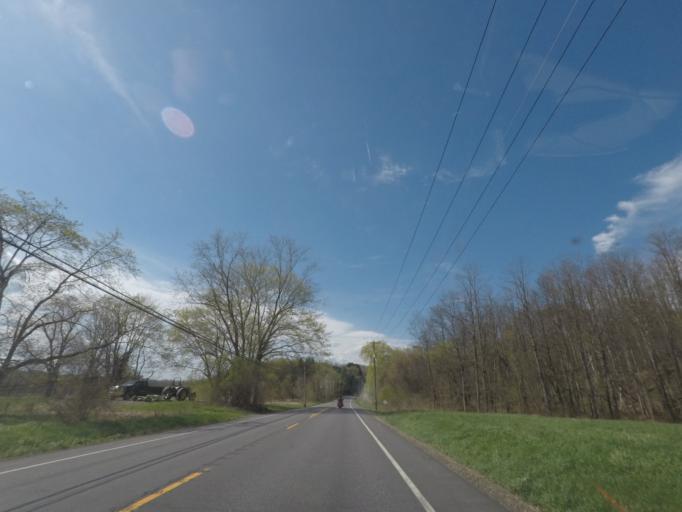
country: US
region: New York
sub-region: Greene County
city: Cairo
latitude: 42.3506
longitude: -74.0458
